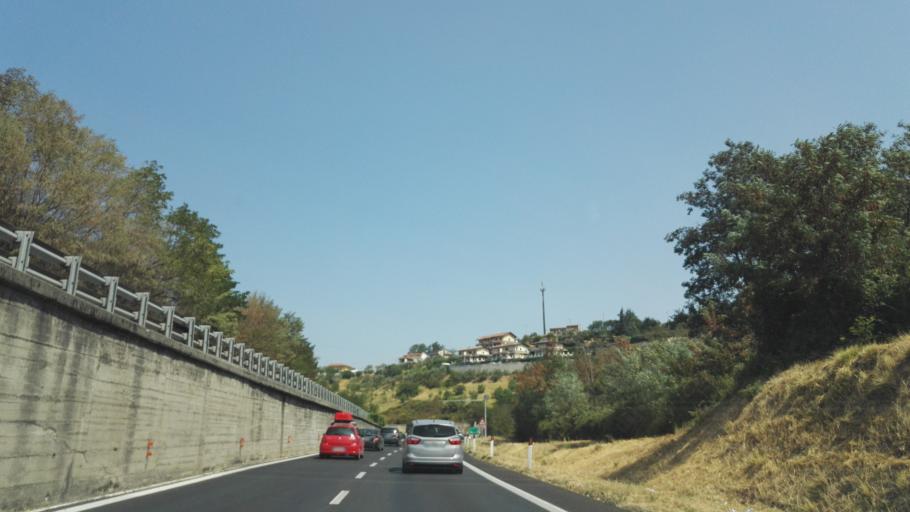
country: IT
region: Calabria
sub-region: Provincia di Cosenza
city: Rosario
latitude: 39.2894
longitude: 16.2393
